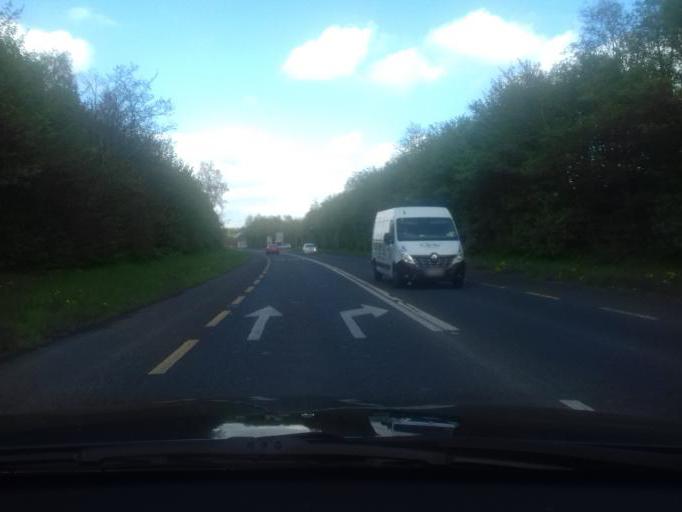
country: IE
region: Leinster
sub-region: Laois
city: Portlaoise
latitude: 53.0460
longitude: -7.2486
